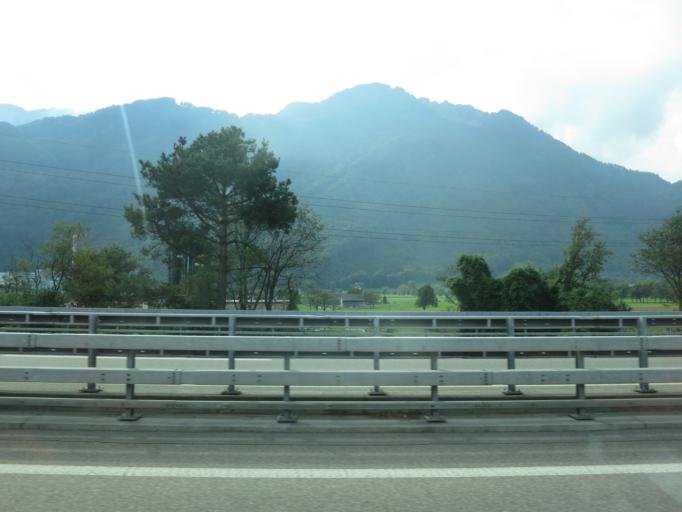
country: CH
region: Saint Gallen
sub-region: Wahlkreis See-Gaster
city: Schanis
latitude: 47.1434
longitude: 9.0461
